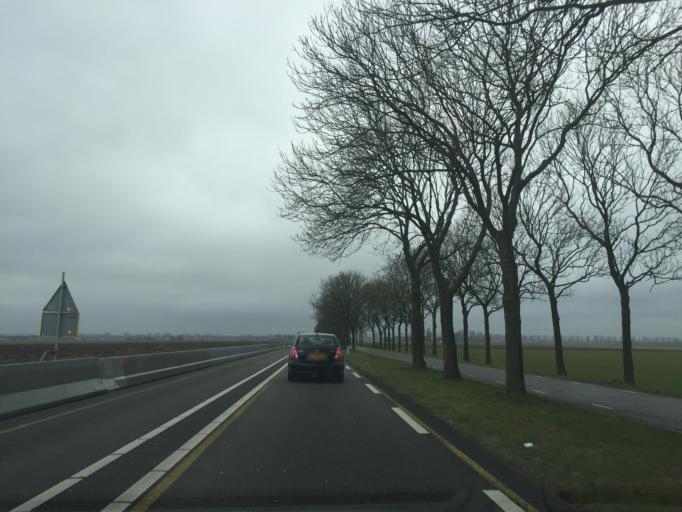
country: NL
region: South Holland
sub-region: Gemeente Kaag en Braassem
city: Oude Wetering
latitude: 52.1811
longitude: 4.6717
